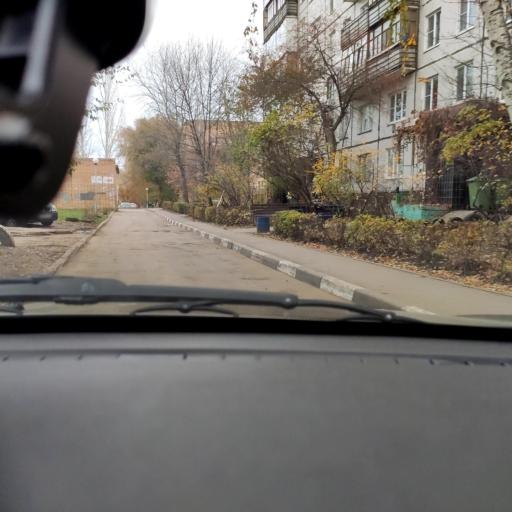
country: RU
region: Samara
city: Tol'yatti
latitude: 53.5208
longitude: 49.3091
